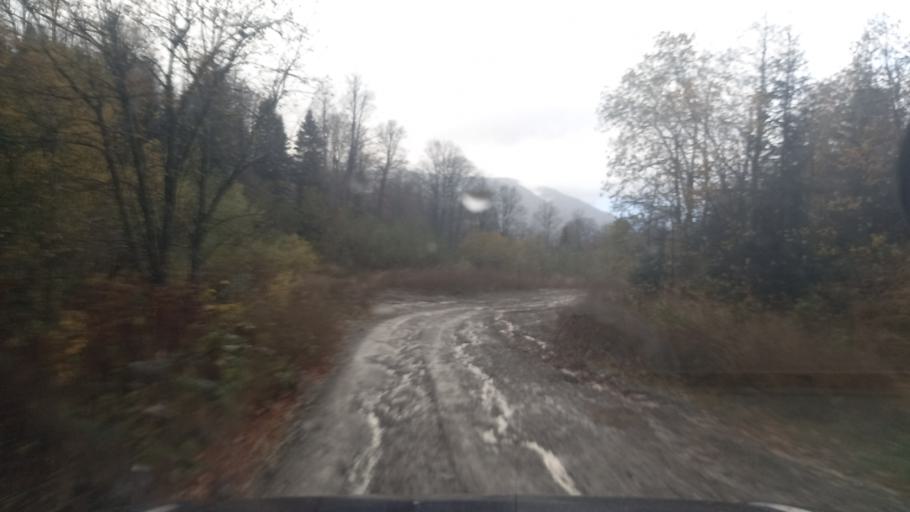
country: RU
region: Krasnodarskiy
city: Dagomys
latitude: 43.9997
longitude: 39.8488
